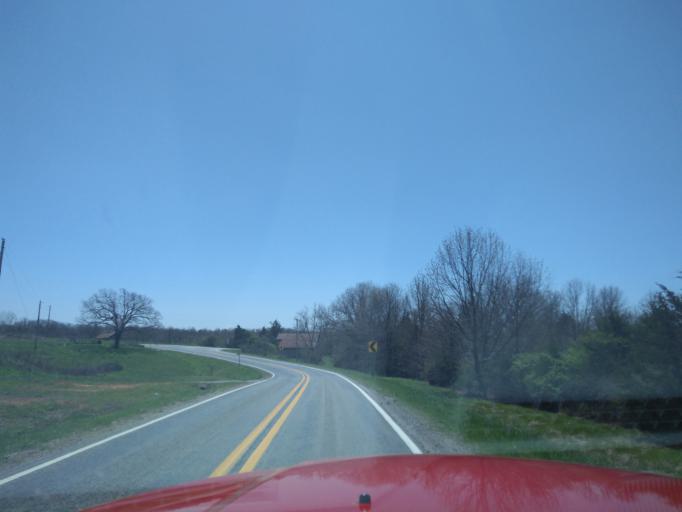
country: US
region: Arkansas
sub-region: Washington County
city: West Fork
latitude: 35.8448
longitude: -94.2756
